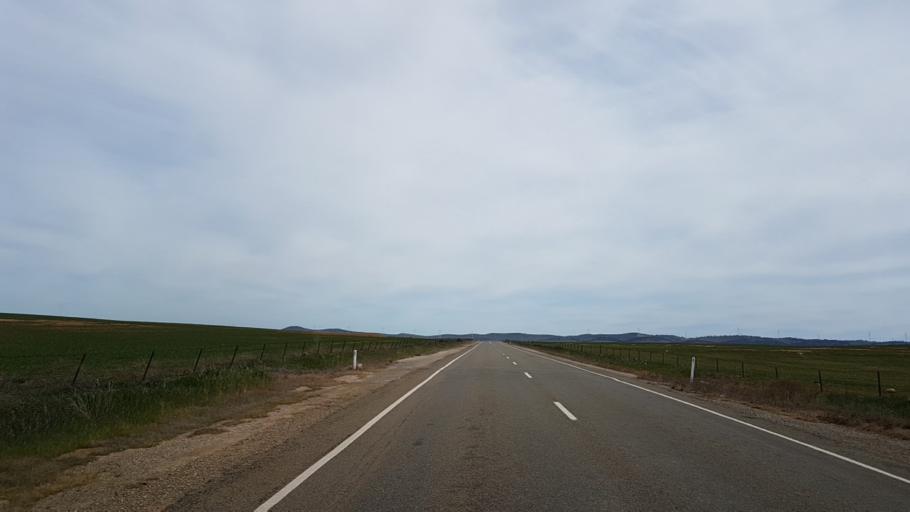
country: AU
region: South Australia
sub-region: Peterborough
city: Peterborough
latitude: -33.0239
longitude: 138.6761
